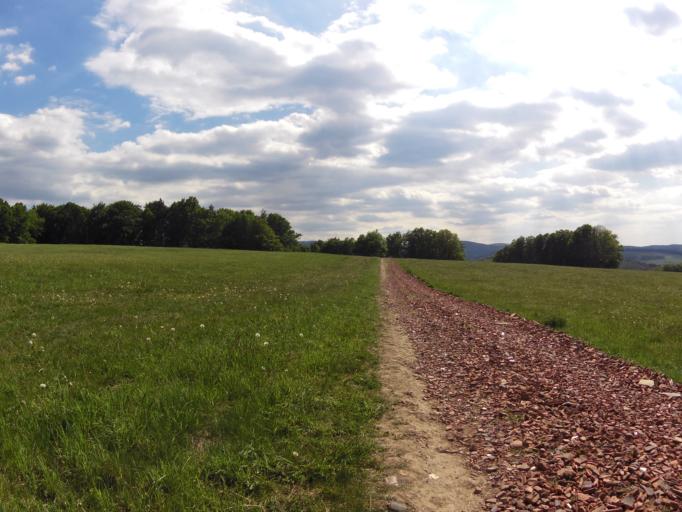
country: DE
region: Thuringia
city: Seebach
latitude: 50.9561
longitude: 10.4287
